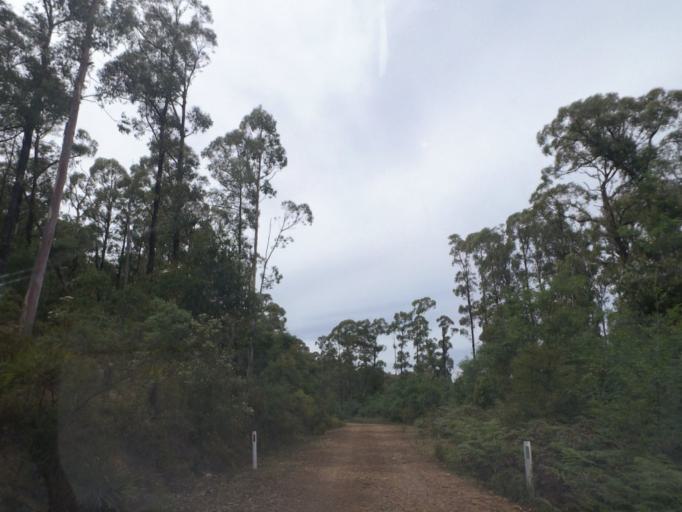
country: AU
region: Victoria
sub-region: Yarra Ranges
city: Healesville
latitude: -37.4347
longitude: 145.5789
